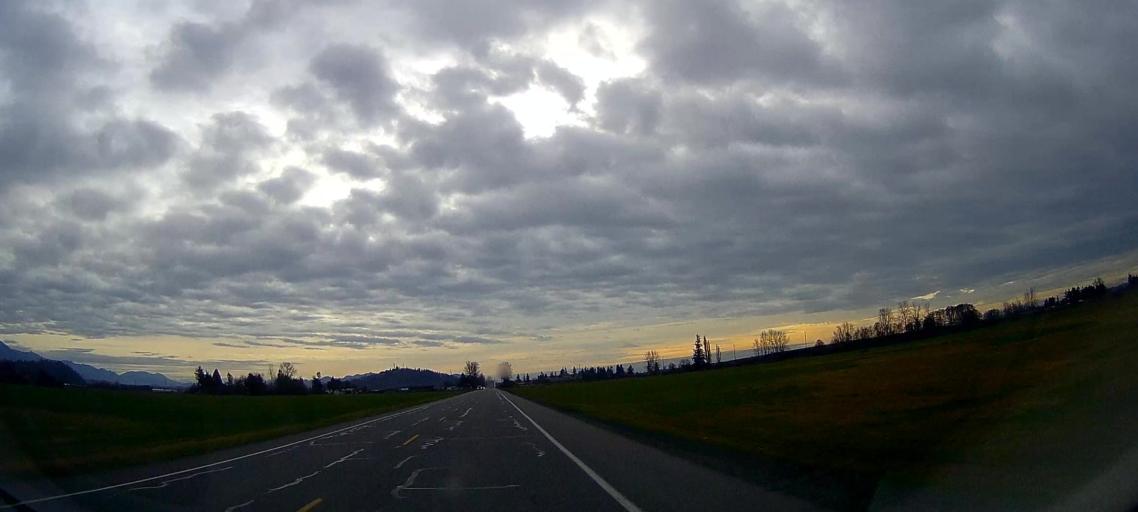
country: US
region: Washington
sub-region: Skagit County
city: Burlington
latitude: 48.5217
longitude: -122.3395
